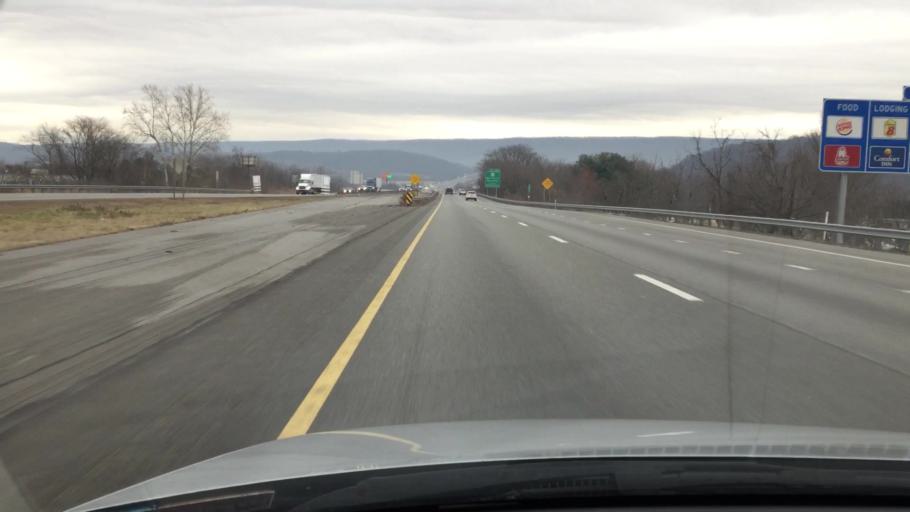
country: US
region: Pennsylvania
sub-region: Columbia County
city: Mifflinville
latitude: 41.0319
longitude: -76.3328
